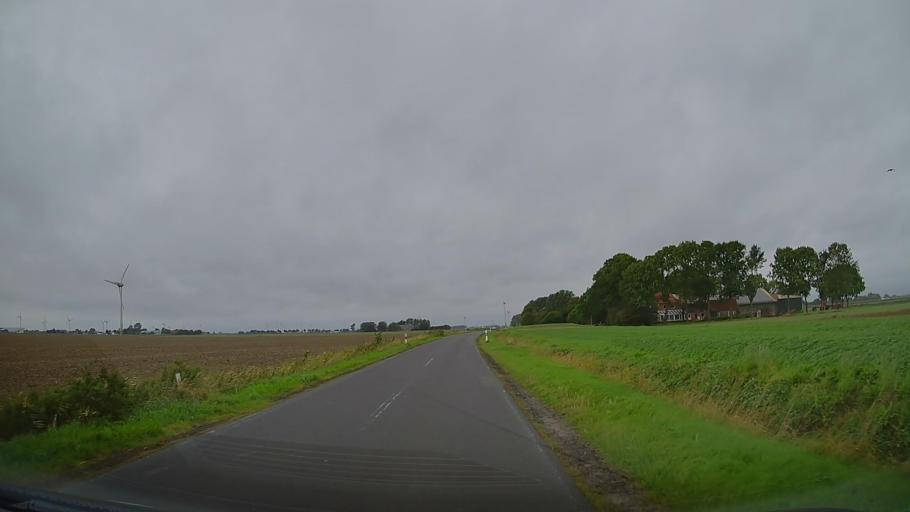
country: DE
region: Schleswig-Holstein
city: Marnerdeich
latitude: 53.9233
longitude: 8.9867
